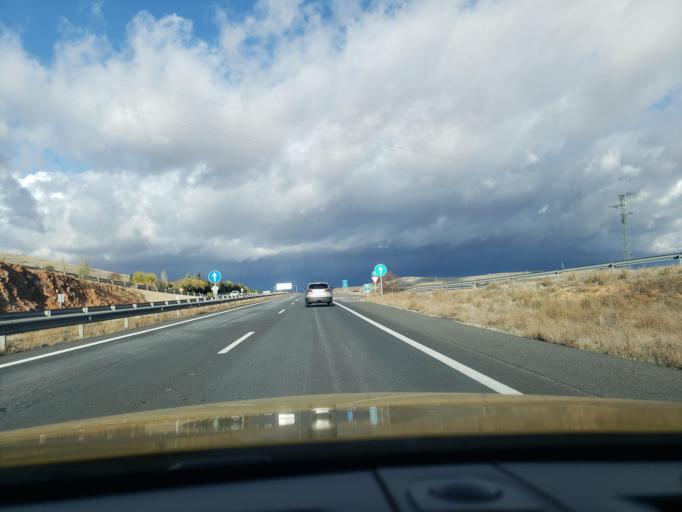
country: ES
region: Castille-La Mancha
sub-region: Provincia de Ciudad Real
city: Valdepenas
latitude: 38.7038
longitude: -3.4223
